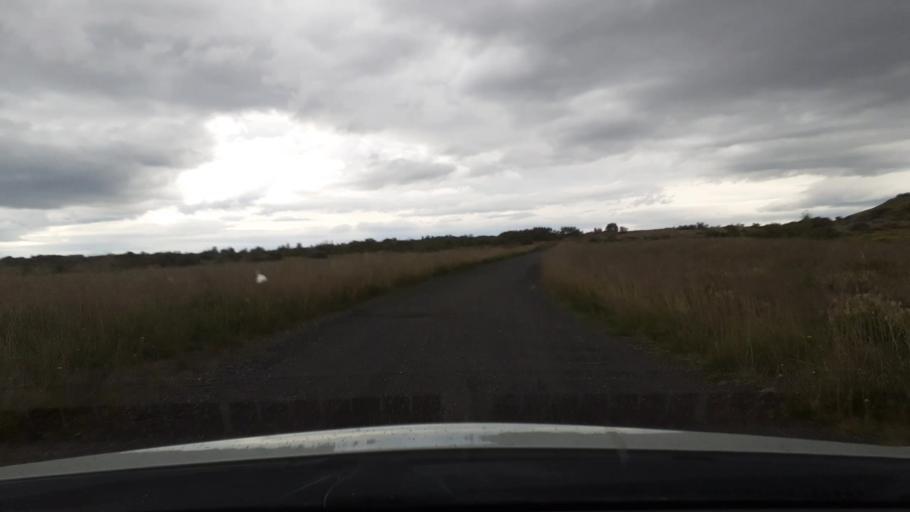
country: IS
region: West
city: Borgarnes
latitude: 64.6385
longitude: -21.7466
